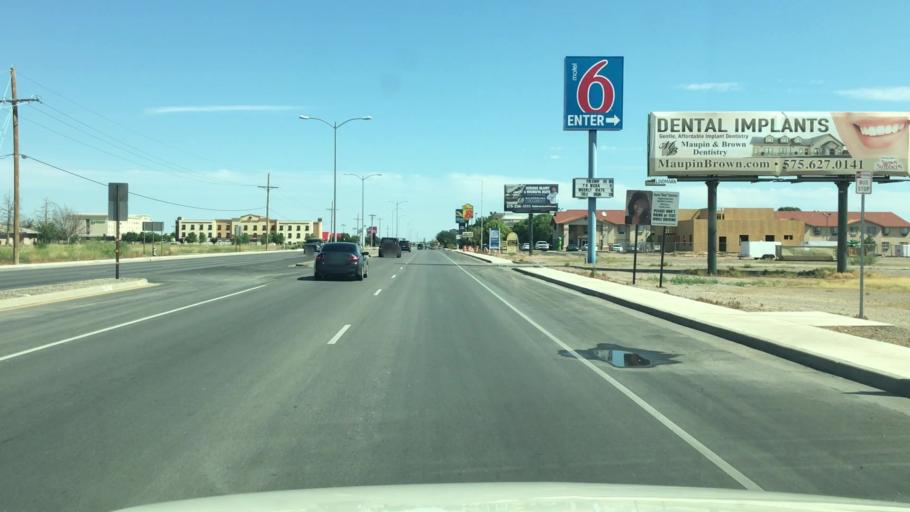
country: US
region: New Mexico
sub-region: Chaves County
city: Roswell
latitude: 33.4385
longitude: -104.5231
